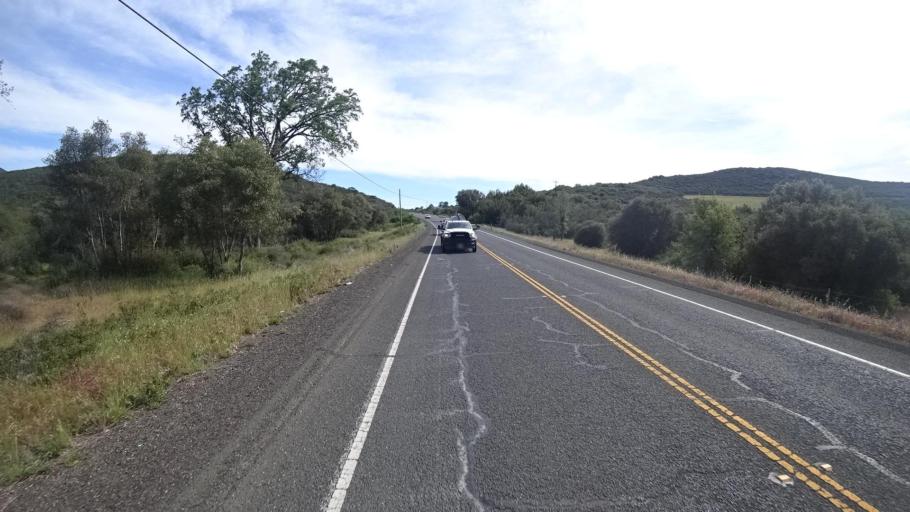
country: US
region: California
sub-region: Lake County
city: Soda Bay
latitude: 38.9437
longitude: -122.7364
